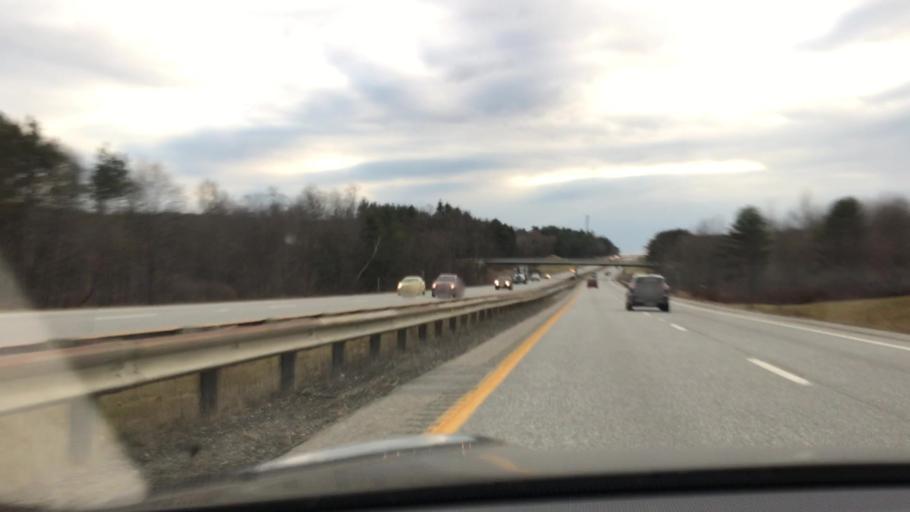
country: US
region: Maine
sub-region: Kennebec County
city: Hallowell
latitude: 44.2794
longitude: -69.8065
